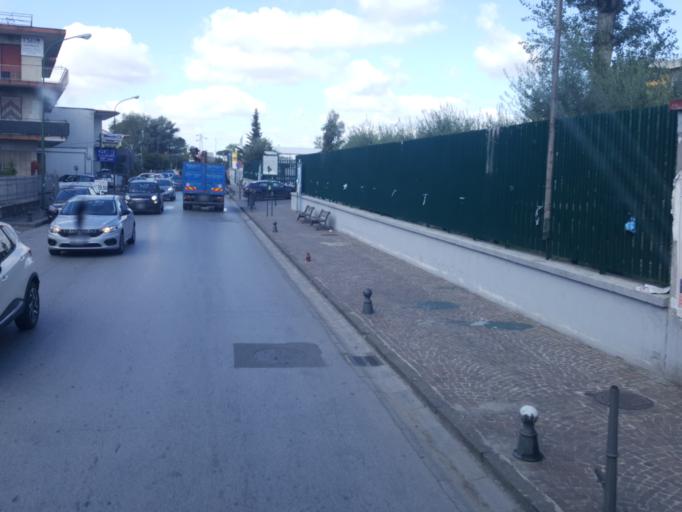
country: IT
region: Campania
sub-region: Provincia di Napoli
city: Nola
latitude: 40.9170
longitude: 14.5222
